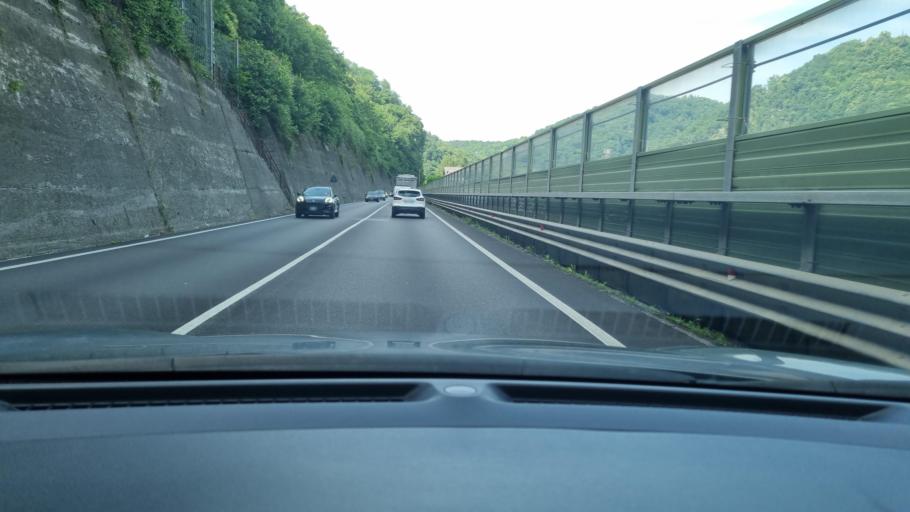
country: IT
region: Lombardy
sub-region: Provincia di Bergamo
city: Villa d'Alme
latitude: 45.7650
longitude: 9.6103
